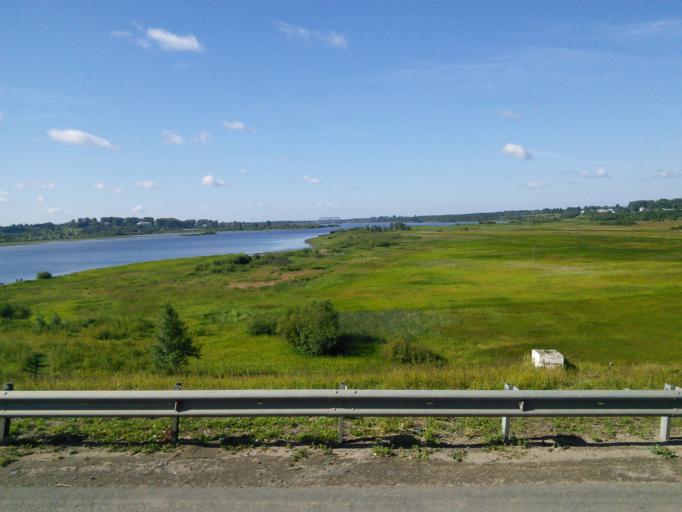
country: RU
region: Vologda
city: Sheksna
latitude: 59.2149
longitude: 38.4917
